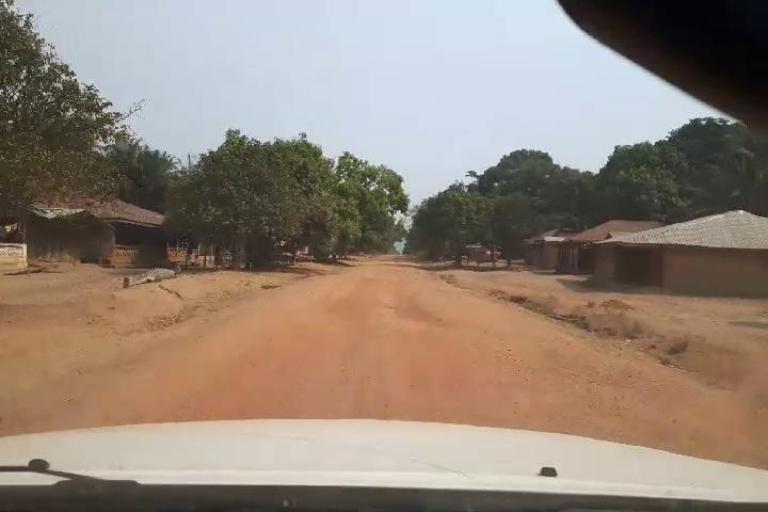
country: SL
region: Northern Province
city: Masingbi
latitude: 8.8768
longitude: -11.8189
